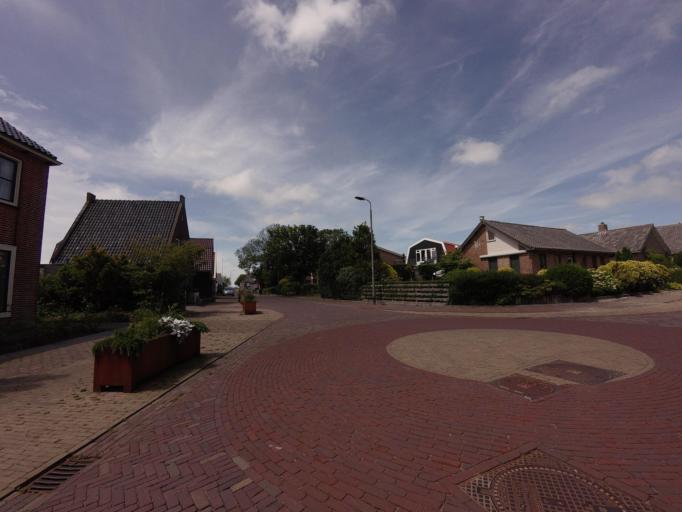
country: NL
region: North Holland
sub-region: Gemeente Texel
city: Den Burg
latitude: 53.0834
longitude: 4.8765
